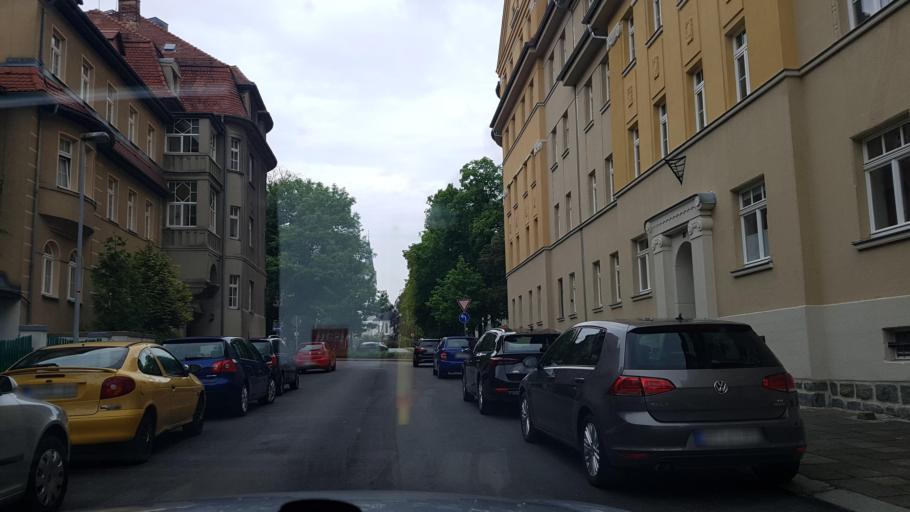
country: DE
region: Saxony
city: Lobau
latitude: 51.0973
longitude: 14.6606
